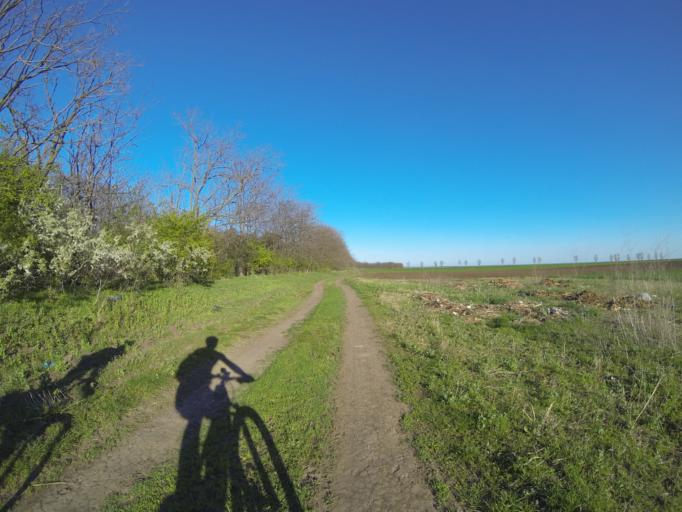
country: RO
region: Dolj
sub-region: Comuna Ceratu
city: Ceratu
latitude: 44.0764
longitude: 23.6861
